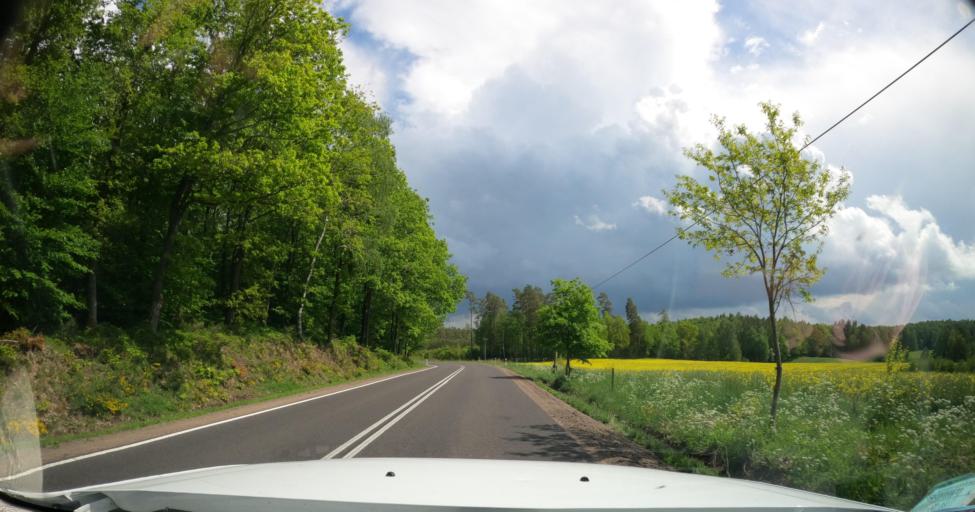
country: PL
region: Pomeranian Voivodeship
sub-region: Powiat bytowski
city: Czarna Dabrowka
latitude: 54.3443
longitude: 17.5947
